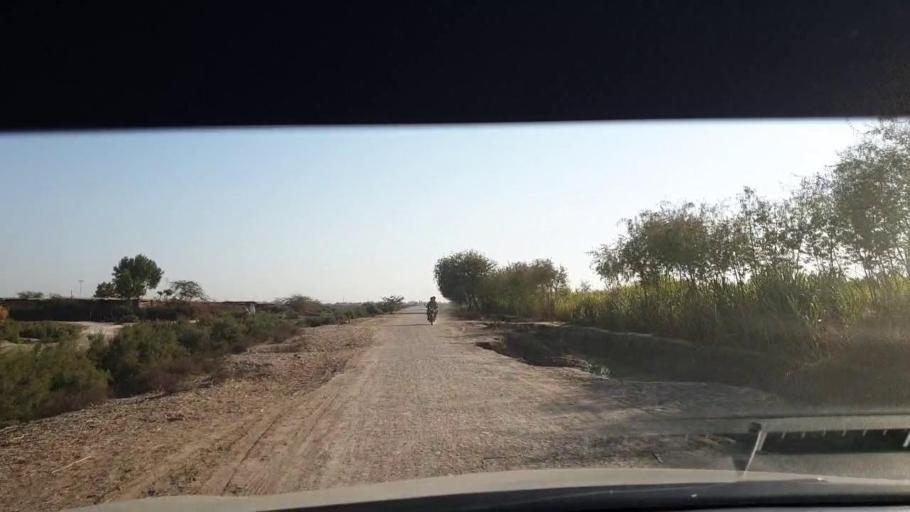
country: PK
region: Sindh
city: Berani
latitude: 25.7949
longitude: 68.9263
